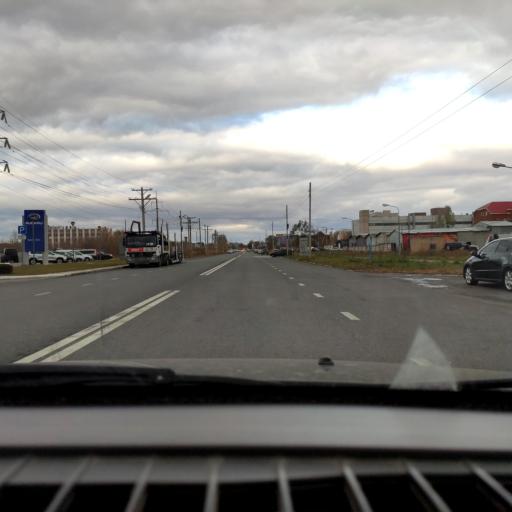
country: RU
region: Samara
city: Tol'yatti
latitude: 53.5541
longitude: 49.2935
